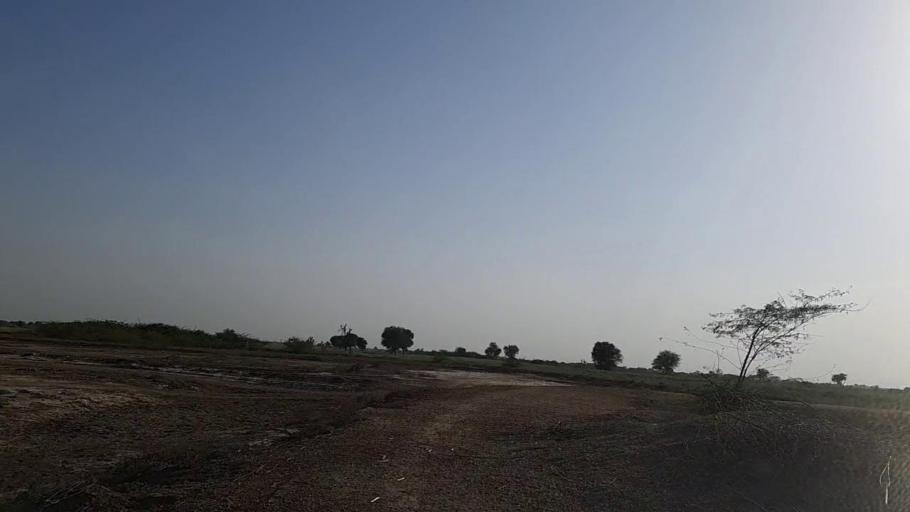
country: PK
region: Sindh
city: Dhoro Naro
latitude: 25.4405
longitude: 69.4897
